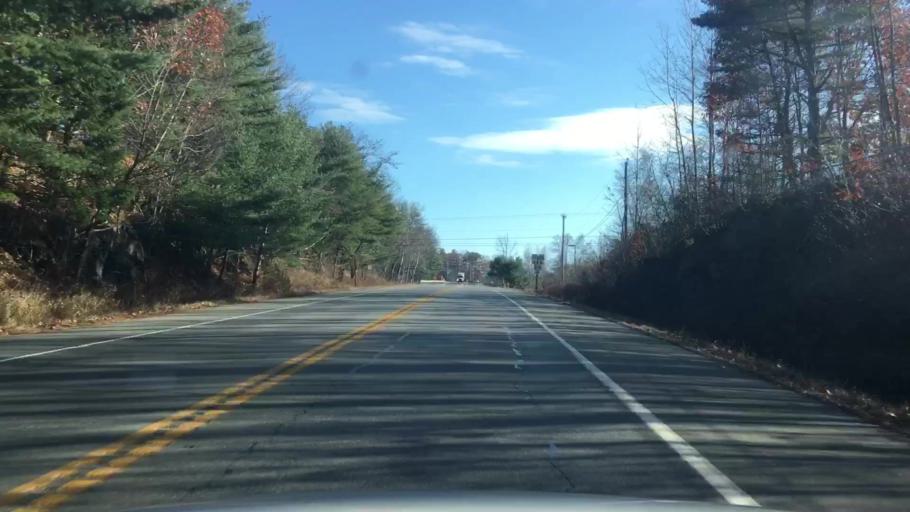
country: US
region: Maine
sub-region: Kennebec County
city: Windsor
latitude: 44.2550
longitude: -69.5478
